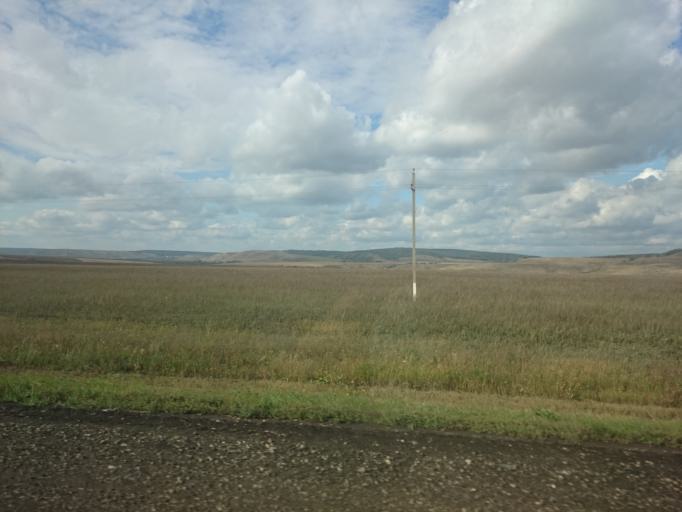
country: RU
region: Samara
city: Kamyshla
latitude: 54.0712
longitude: 52.1919
